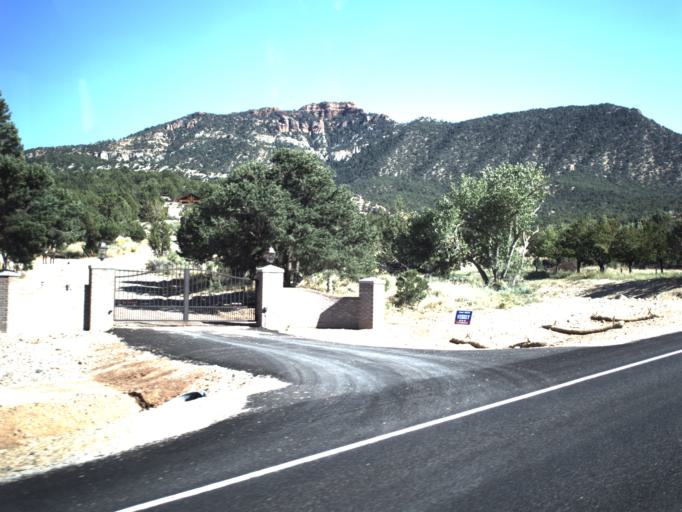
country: US
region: Utah
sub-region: Iron County
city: Parowan
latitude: 37.8347
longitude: -112.8174
